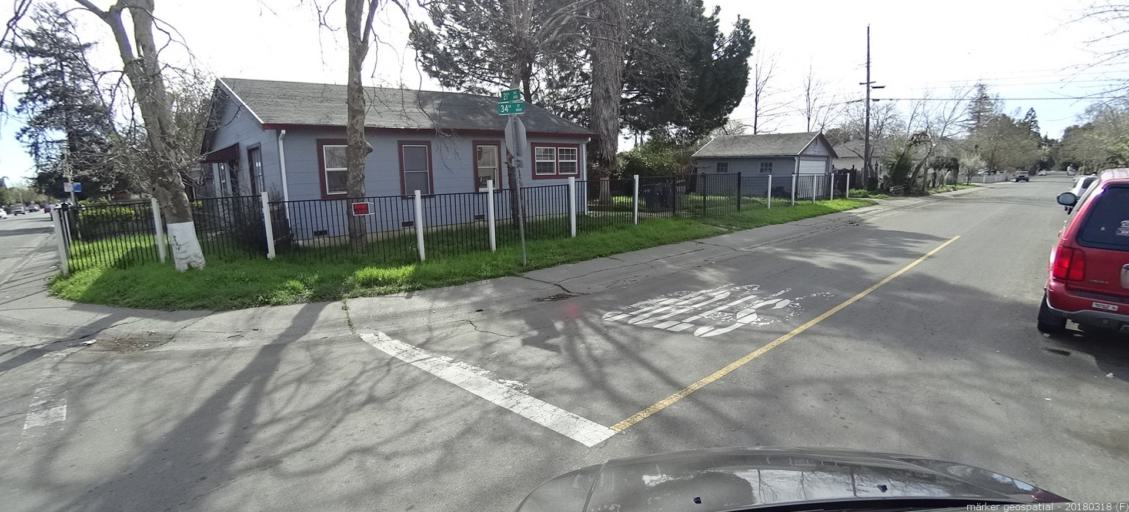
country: US
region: California
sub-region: Sacramento County
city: Parkway
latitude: 38.5336
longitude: -121.4707
